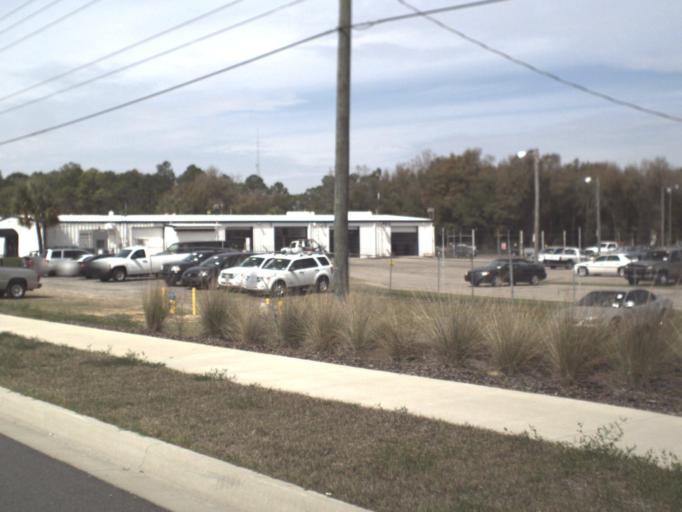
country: US
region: Florida
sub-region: Leon County
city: Tallahassee
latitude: 30.3759
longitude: -84.2827
